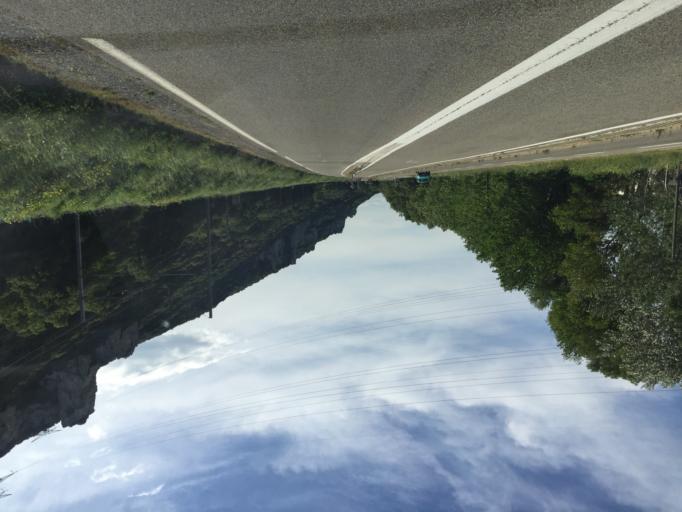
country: FR
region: Rhone-Alpes
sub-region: Departement de l'Ardeche
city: Cruas
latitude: 44.6365
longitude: 4.7468
